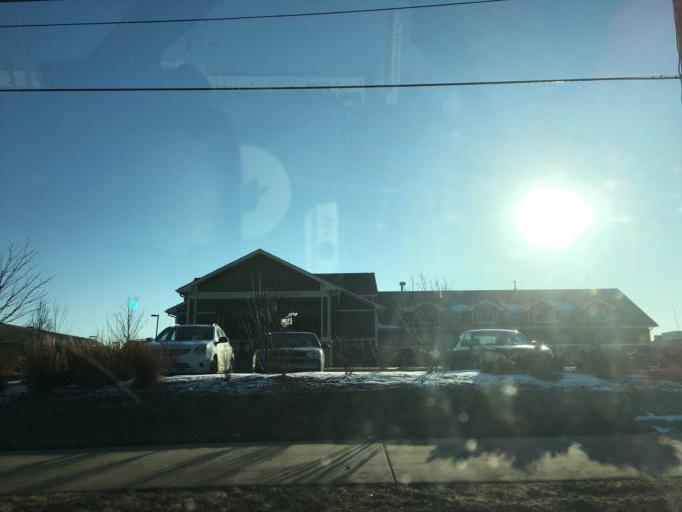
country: US
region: Illinois
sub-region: Cook County
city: Hoffman Estates
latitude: 42.0525
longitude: -88.0795
